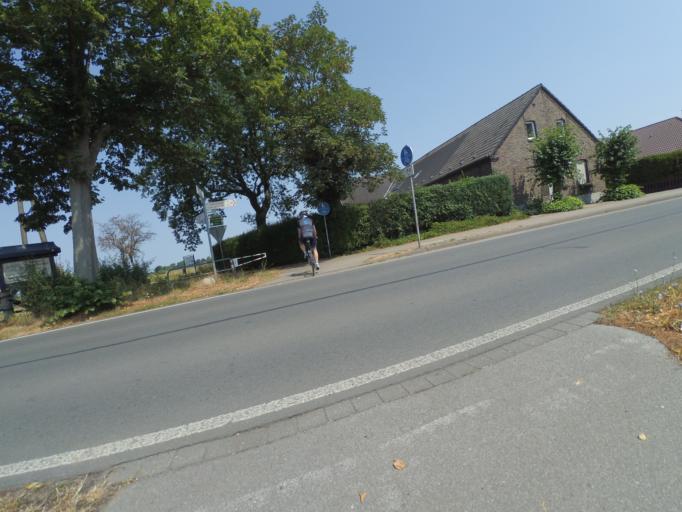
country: DE
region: North Rhine-Westphalia
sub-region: Regierungsbezirk Dusseldorf
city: Mehrhoog
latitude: 51.7302
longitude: 6.4686
